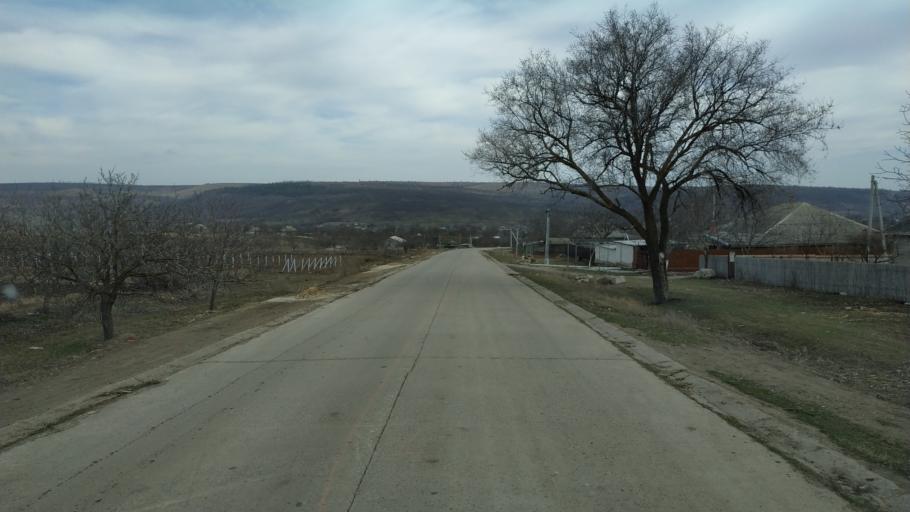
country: MD
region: Nisporeni
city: Nisporeni
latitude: 46.9291
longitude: 28.2560
